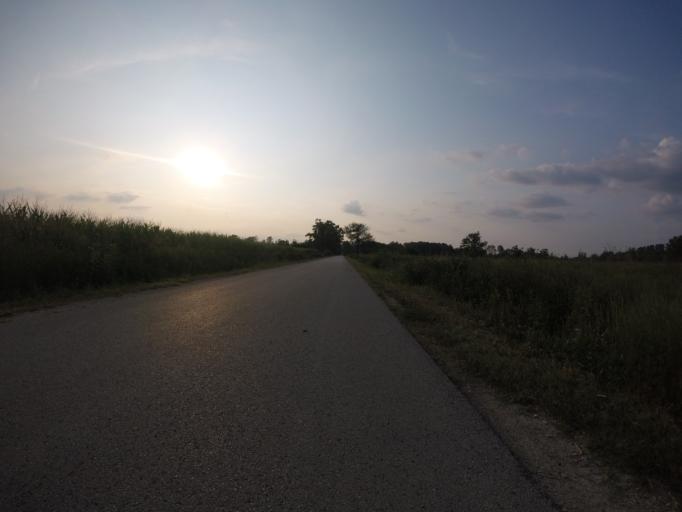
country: HR
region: Zagrebacka
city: Kuce
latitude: 45.7318
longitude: 16.1911
